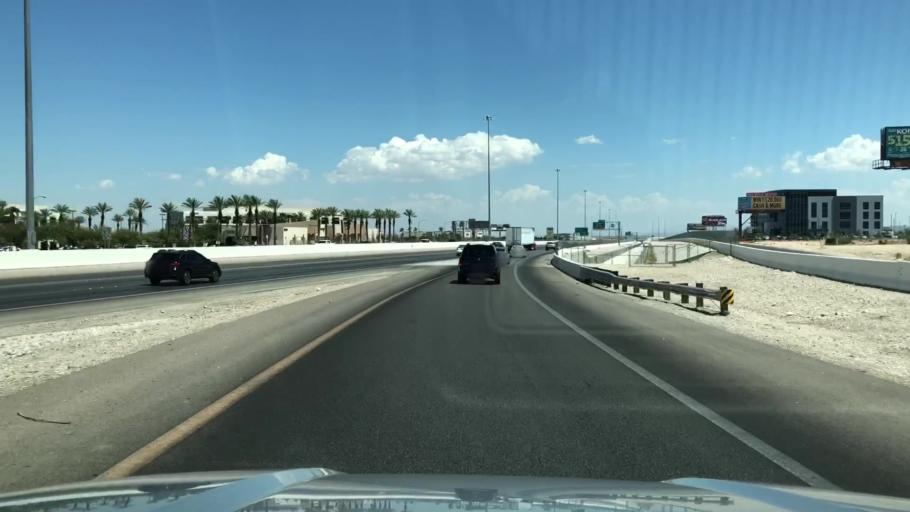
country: US
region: Nevada
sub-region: Clark County
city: Spring Valley
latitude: 36.0659
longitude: -115.2759
